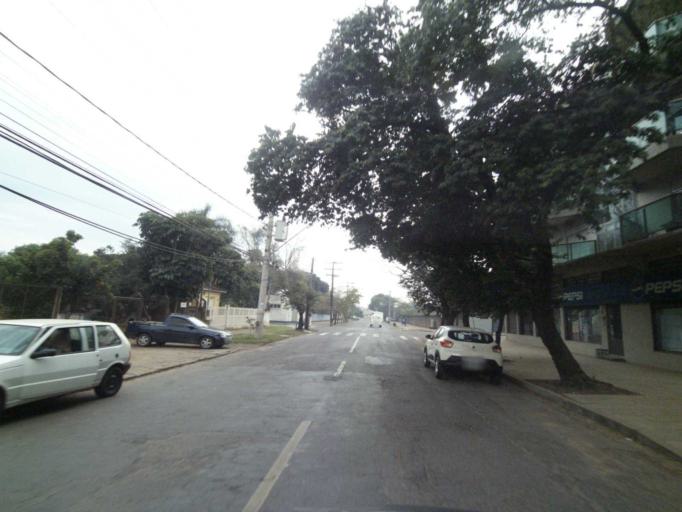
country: BR
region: Rio Grande do Sul
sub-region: Sao Leopoldo
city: Sao Leopoldo
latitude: -29.7746
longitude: -51.1561
